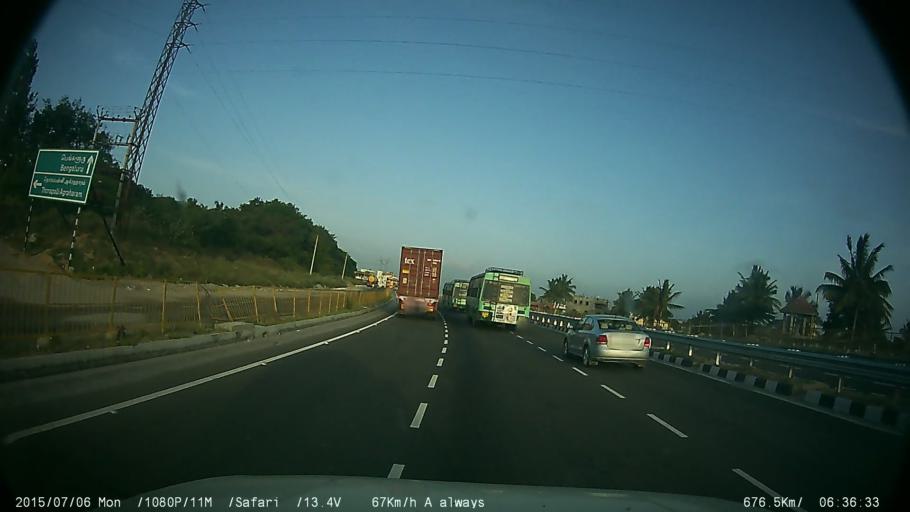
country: IN
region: Tamil Nadu
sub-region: Krishnagiri
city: Hosur
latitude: 12.7115
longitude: 77.8932
